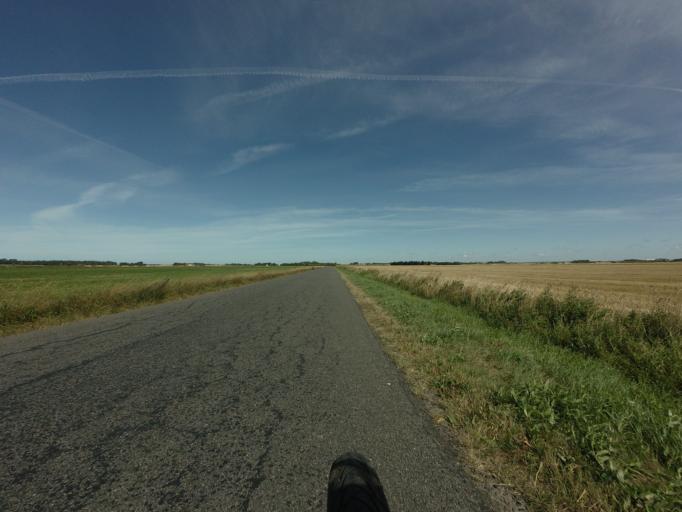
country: DK
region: North Denmark
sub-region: Bronderslev Kommune
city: Bronderslev
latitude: 57.3114
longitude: 9.8110
